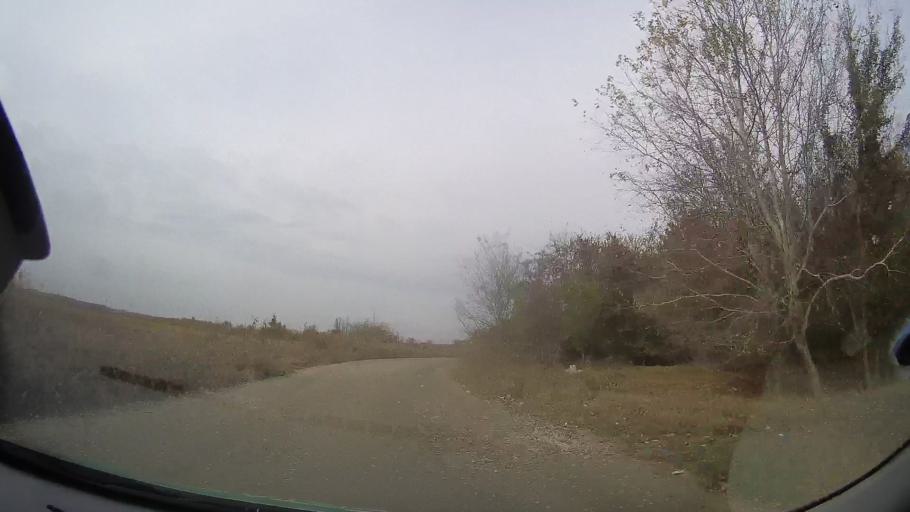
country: RO
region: Ialomita
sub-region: Comuna Fierbinti-Targ
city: Fierbinti-Targ
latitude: 44.6787
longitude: 26.3477
